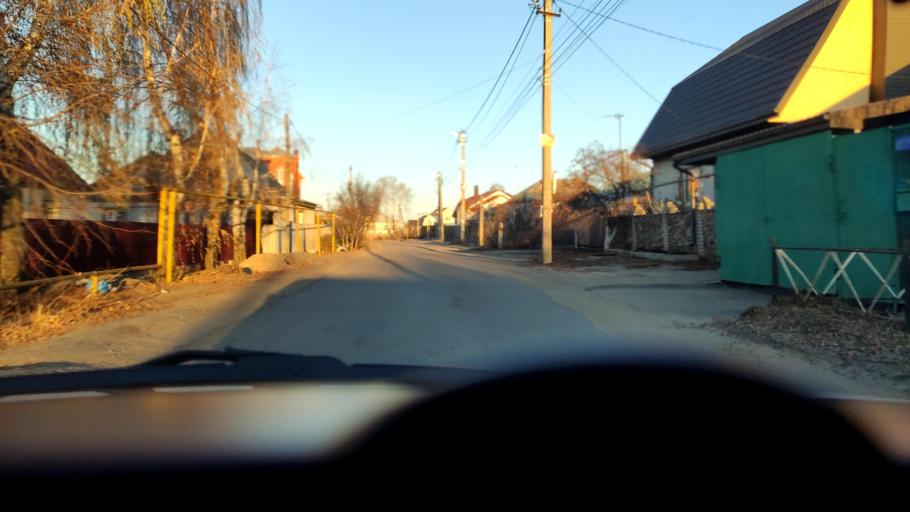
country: RU
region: Voronezj
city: Podgornoye
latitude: 51.7378
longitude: 39.1561
